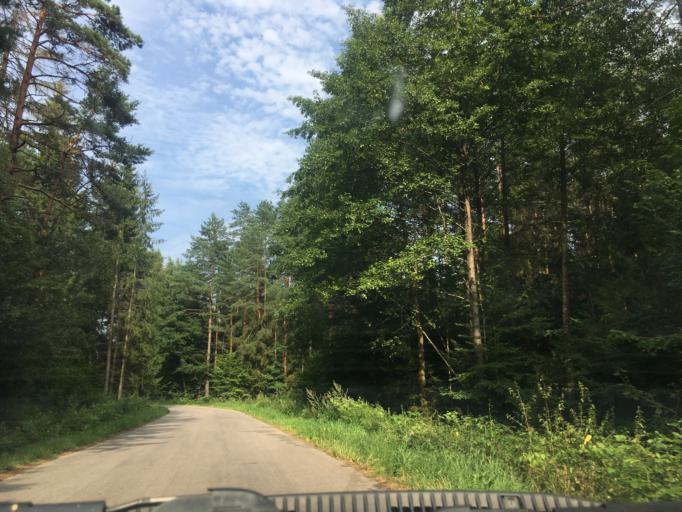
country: PL
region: Podlasie
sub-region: Powiat hajnowski
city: Bialowieza
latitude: 52.8824
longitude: 23.8431
